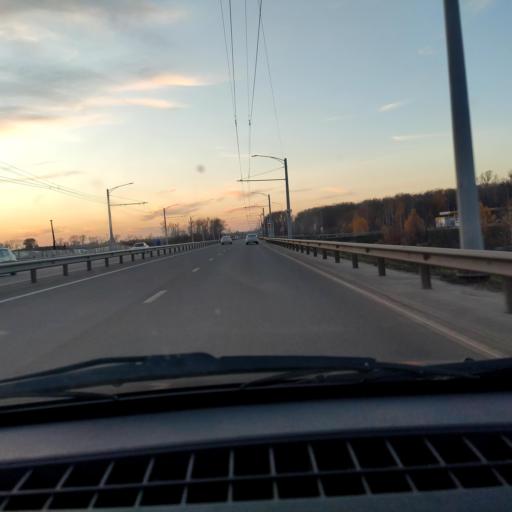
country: RU
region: Bashkortostan
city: Mikhaylovka
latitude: 54.7722
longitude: 55.9039
